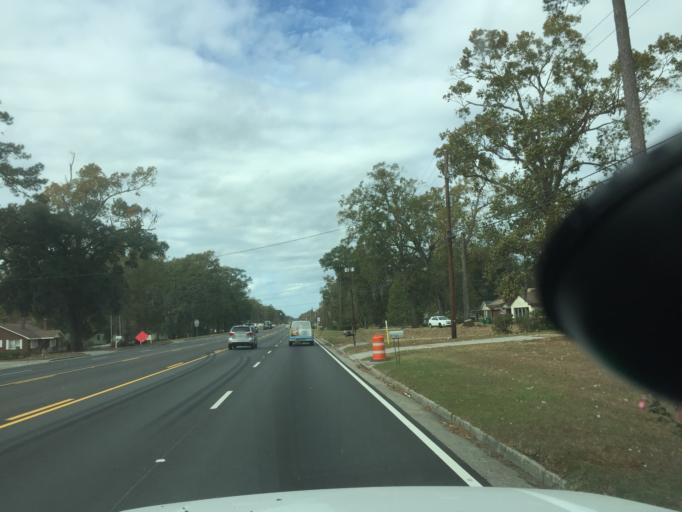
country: US
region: Georgia
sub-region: Chatham County
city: Garden City
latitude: 32.0888
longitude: -81.1791
